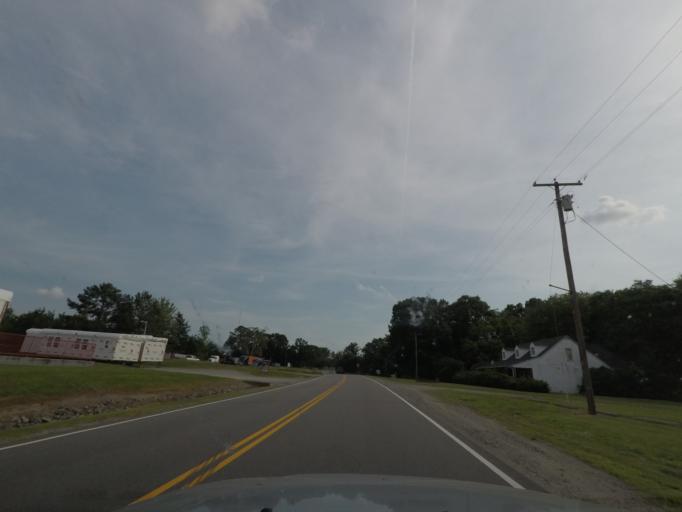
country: US
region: Virginia
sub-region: Mecklenburg County
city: Chase City
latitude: 36.8602
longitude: -78.5890
